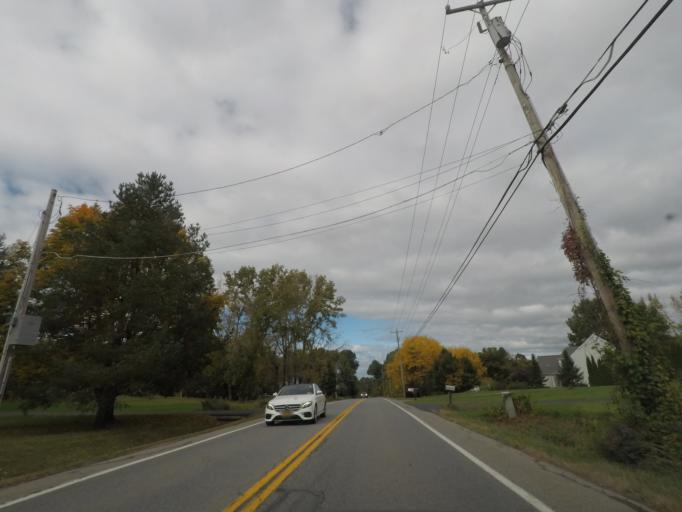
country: US
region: New York
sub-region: Saratoga County
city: Country Knolls
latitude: 42.8867
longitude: -73.7673
